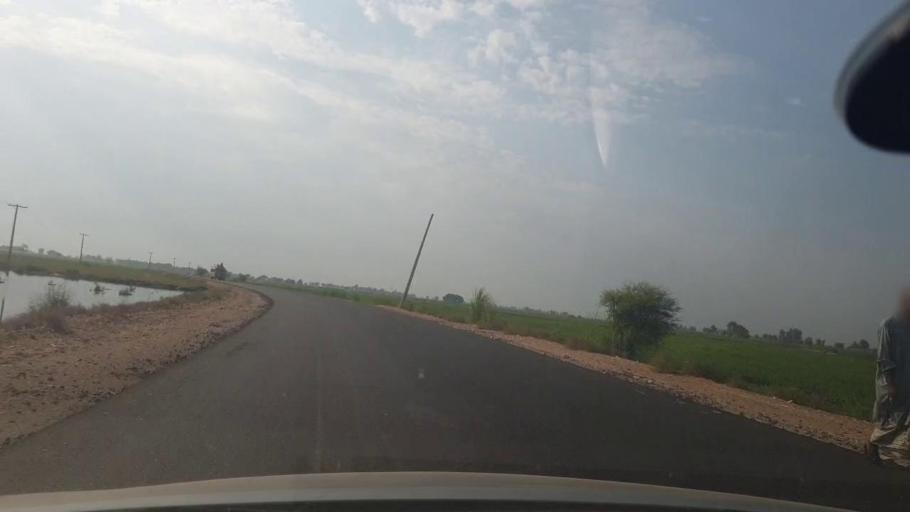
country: PK
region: Sindh
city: Jacobabad
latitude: 28.1004
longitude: 68.3268
